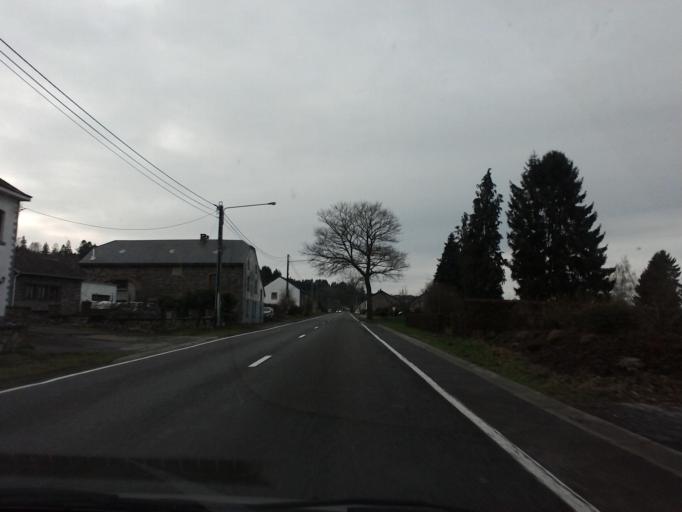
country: BE
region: Wallonia
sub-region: Province de Liege
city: Lierneux
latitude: 50.2522
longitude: 5.8078
